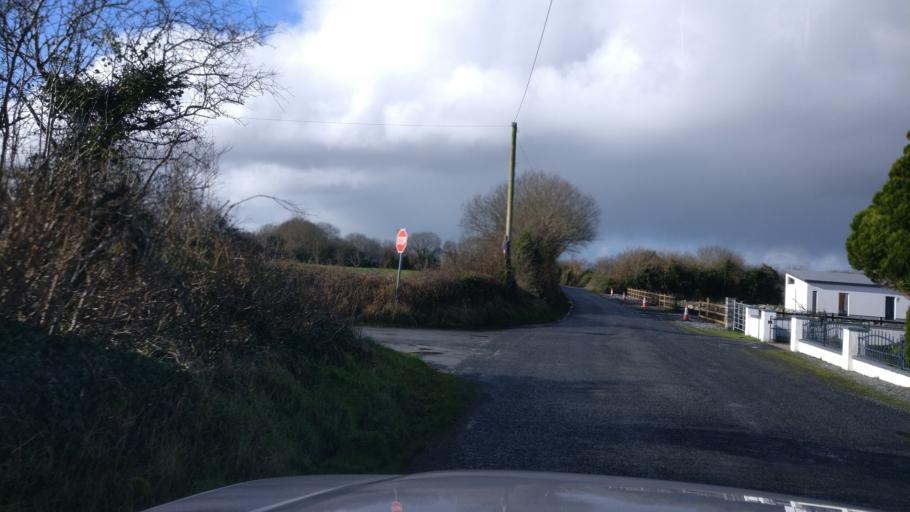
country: IE
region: Connaught
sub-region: County Galway
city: Athenry
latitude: 53.2385
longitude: -8.8046
